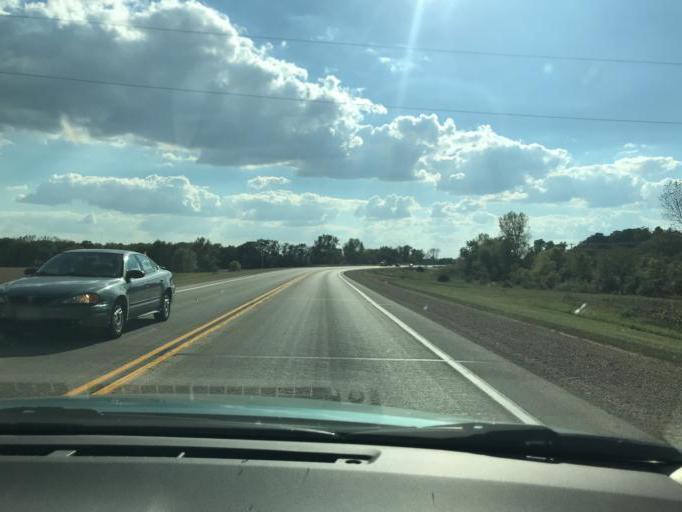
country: US
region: Wisconsin
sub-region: Green County
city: Brodhead
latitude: 42.5891
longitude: -89.4007
